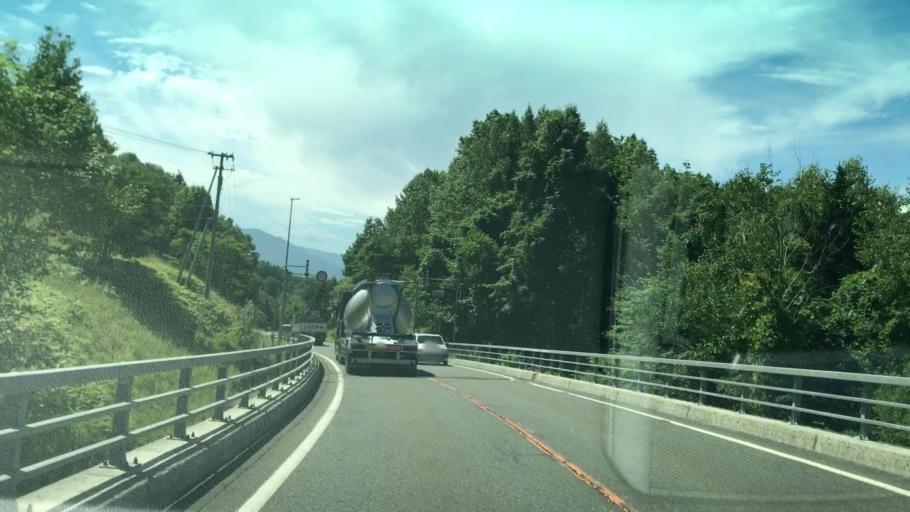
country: JP
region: Hokkaido
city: Shimo-furano
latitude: 42.8986
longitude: 142.4357
